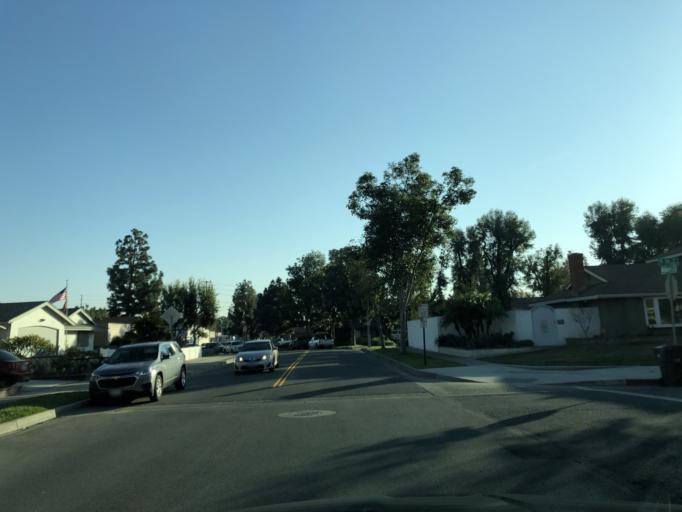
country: US
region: California
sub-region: Orange County
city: Tustin
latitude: 33.7619
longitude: -117.8441
